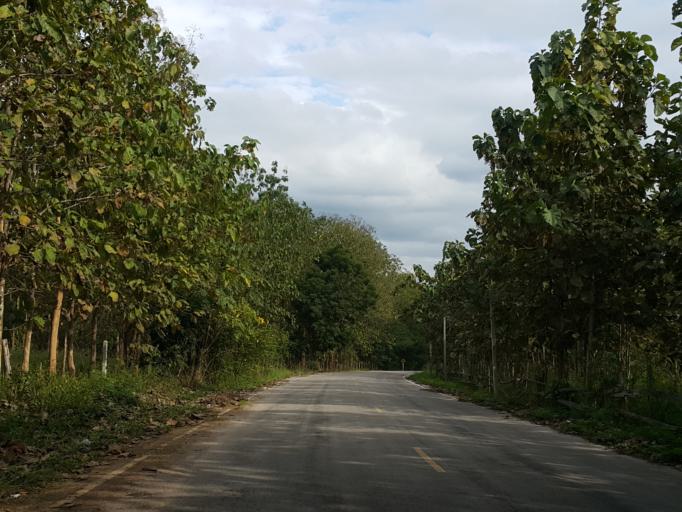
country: TH
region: Lampang
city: Chae Hom
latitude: 18.6531
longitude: 99.5342
